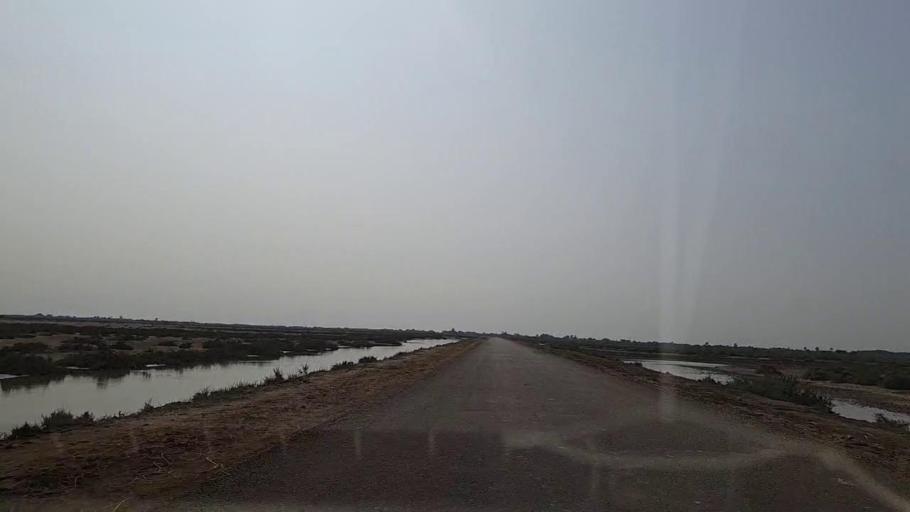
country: PK
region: Sindh
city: Chuhar Jamali
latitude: 24.2065
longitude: 67.8554
